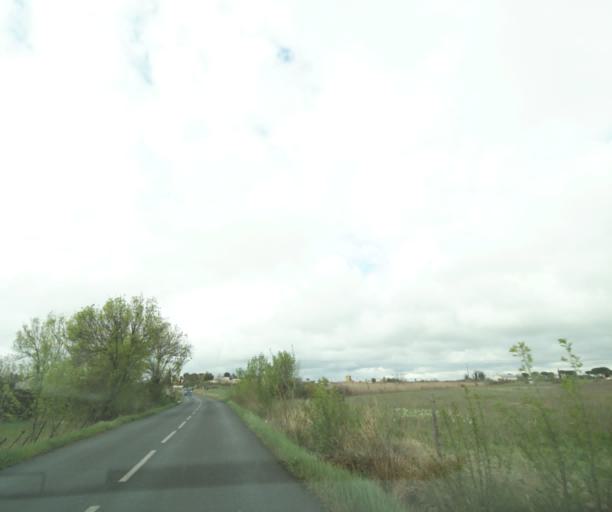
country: FR
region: Languedoc-Roussillon
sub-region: Departement de l'Herault
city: Saussan
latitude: 43.5619
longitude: 3.7757
